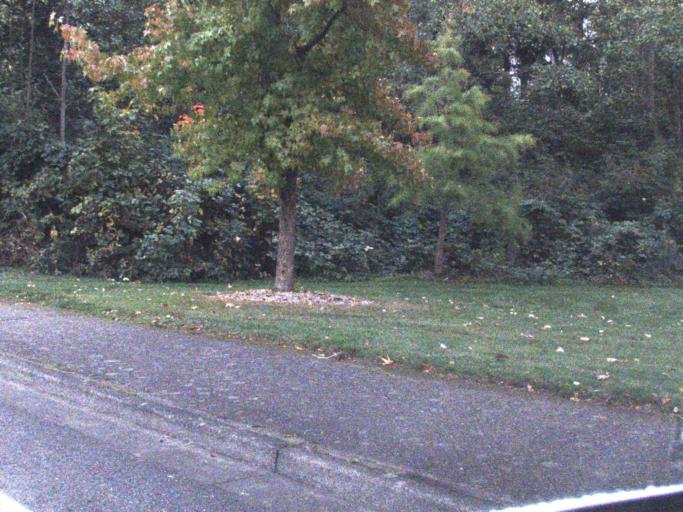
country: US
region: Washington
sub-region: Whatcom County
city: Bellingham
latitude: 48.7161
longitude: -122.4963
